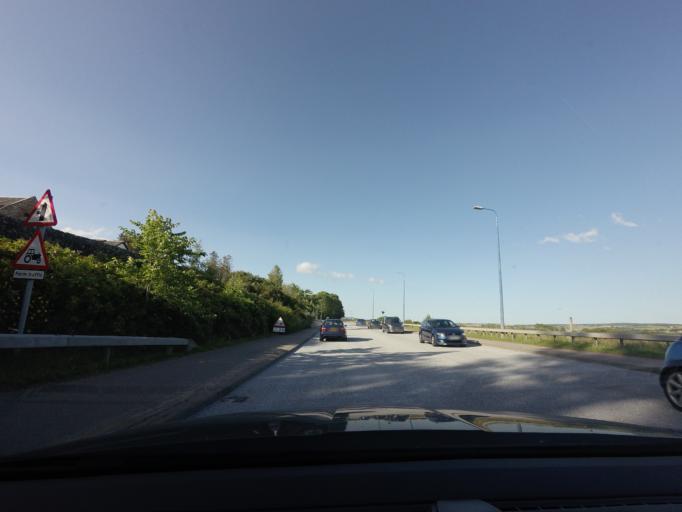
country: GB
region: Scotland
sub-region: Highland
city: Dingwall
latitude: 57.5869
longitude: -4.4275
